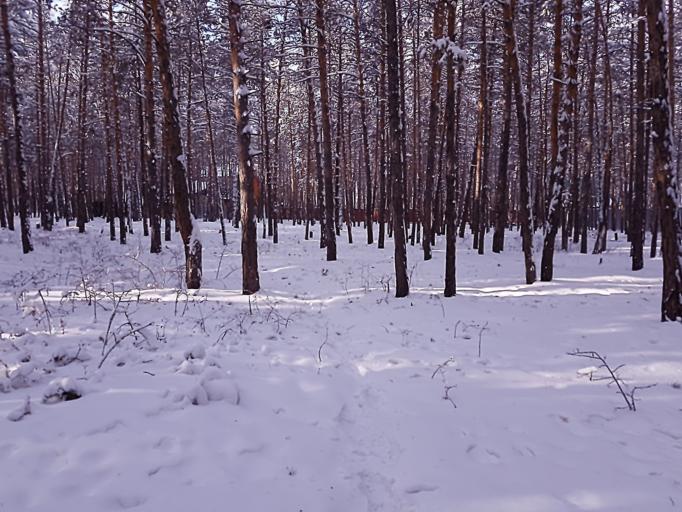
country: RU
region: Sakha
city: Yakutsk
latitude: 62.0238
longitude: 129.6540
